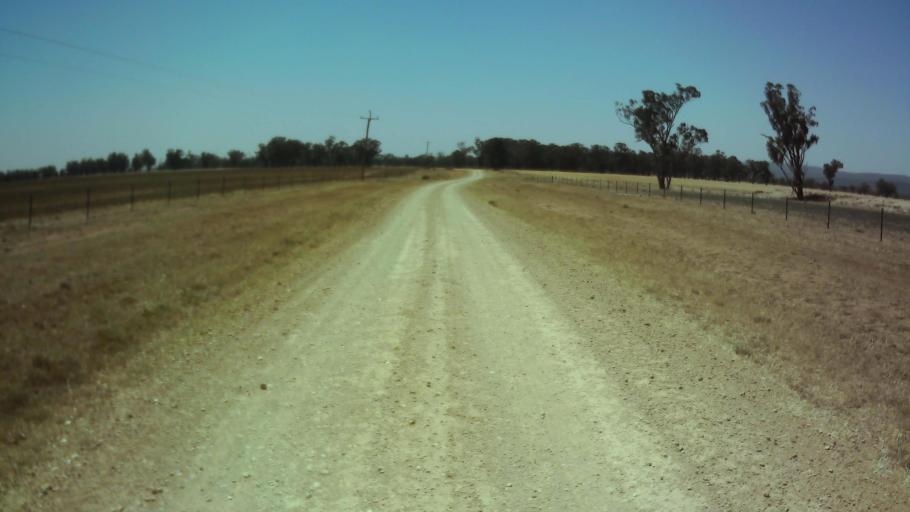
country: AU
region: New South Wales
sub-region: Weddin
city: Grenfell
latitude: -34.0241
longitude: 147.9008
